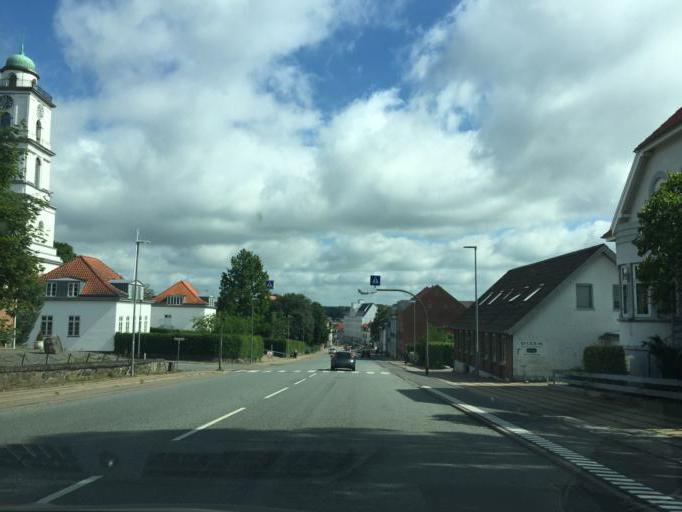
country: DK
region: South Denmark
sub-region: Kolding Kommune
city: Kolding
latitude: 55.4824
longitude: 9.4694
